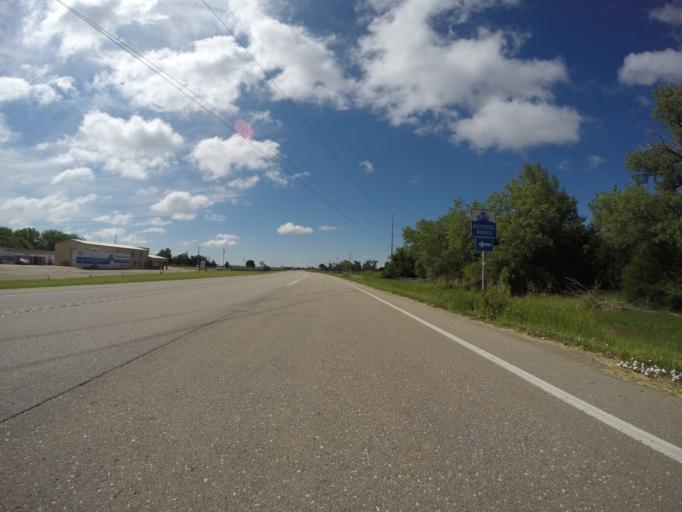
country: US
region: Nebraska
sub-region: Buffalo County
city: Kearney
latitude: 40.6540
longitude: -99.0862
